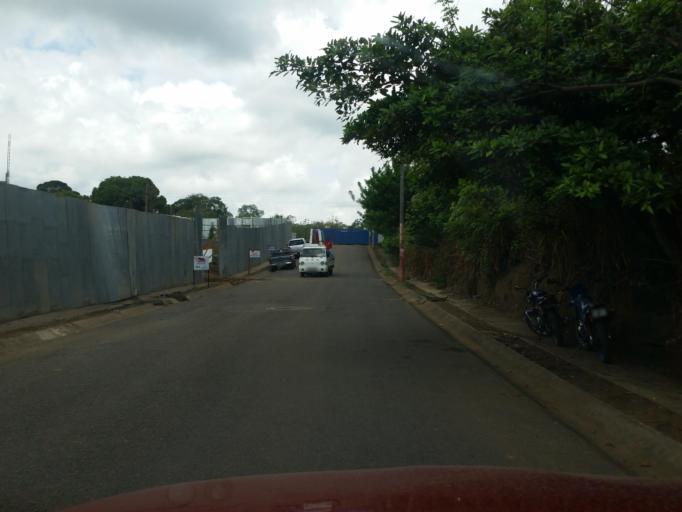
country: NI
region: Masaya
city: Ticuantepe
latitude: 12.0705
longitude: -86.2374
